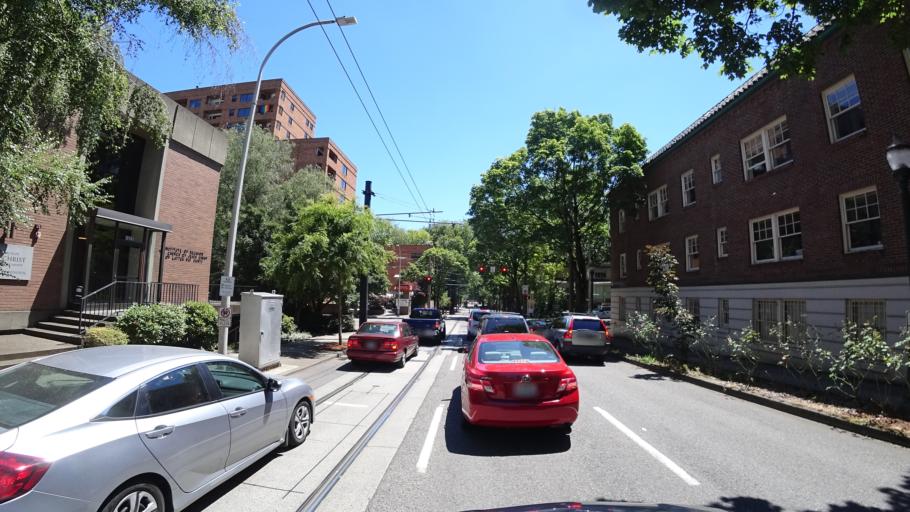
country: US
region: Oregon
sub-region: Multnomah County
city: Portland
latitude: 45.5142
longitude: -122.6859
